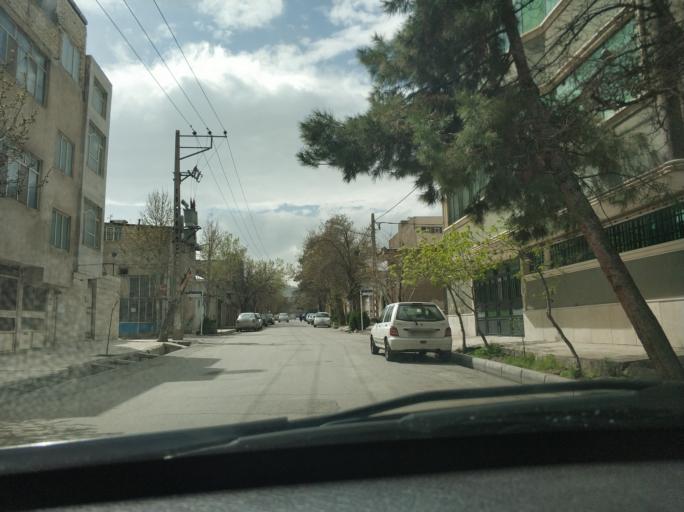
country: IR
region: Razavi Khorasan
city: Mashhad
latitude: 36.2738
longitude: 59.5724
